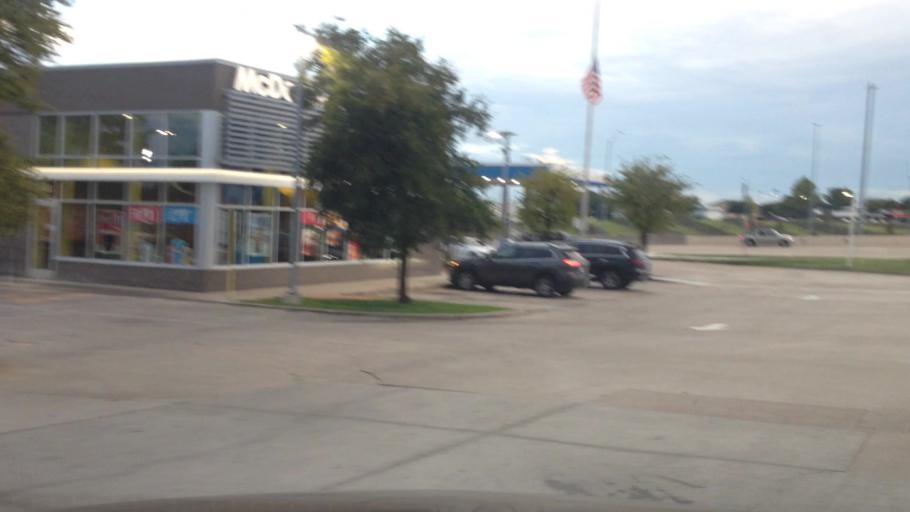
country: US
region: Texas
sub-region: Tarrant County
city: Grapevine
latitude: 32.9248
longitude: -97.0781
